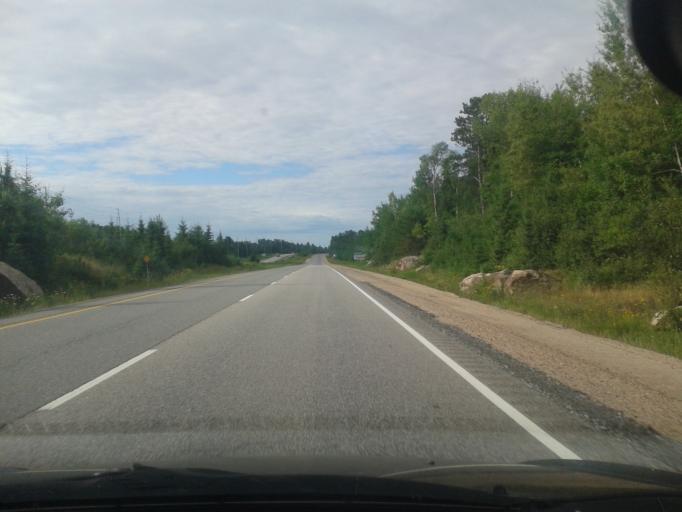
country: CA
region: Ontario
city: Powassan
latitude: 46.1399
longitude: -79.3604
